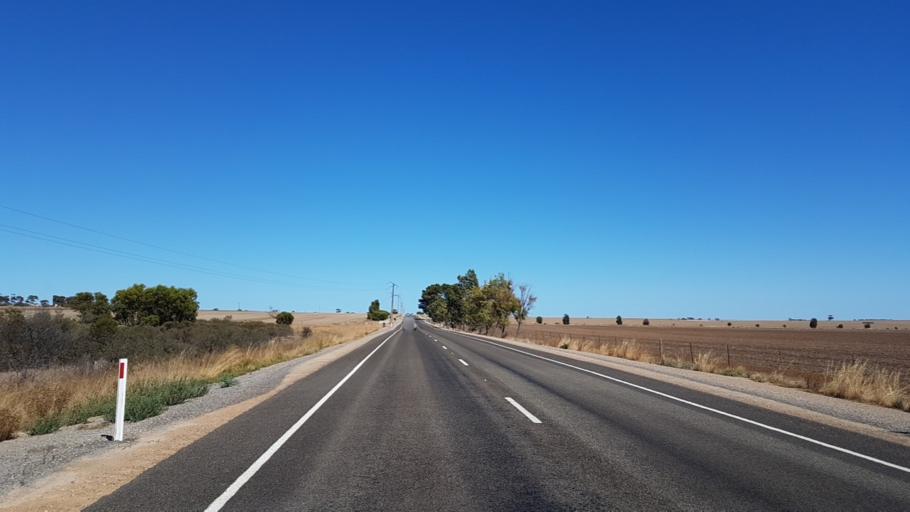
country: AU
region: South Australia
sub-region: Copper Coast
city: Kadina
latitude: -34.0439
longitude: 137.9384
